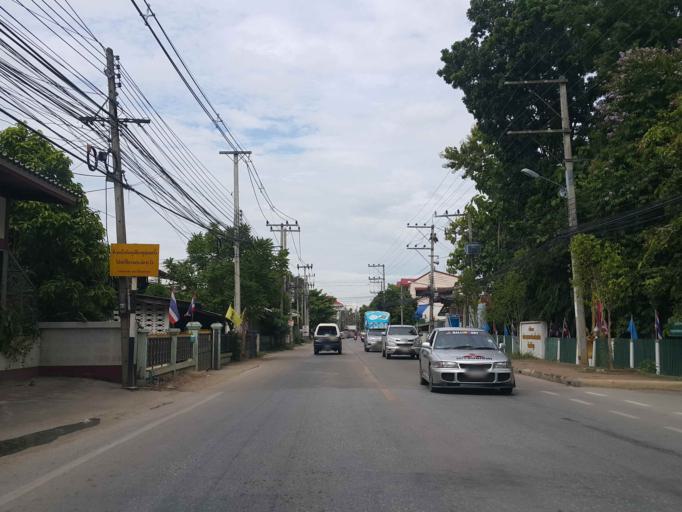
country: TH
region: Lamphun
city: Lamphun
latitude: 18.5704
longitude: 98.9980
